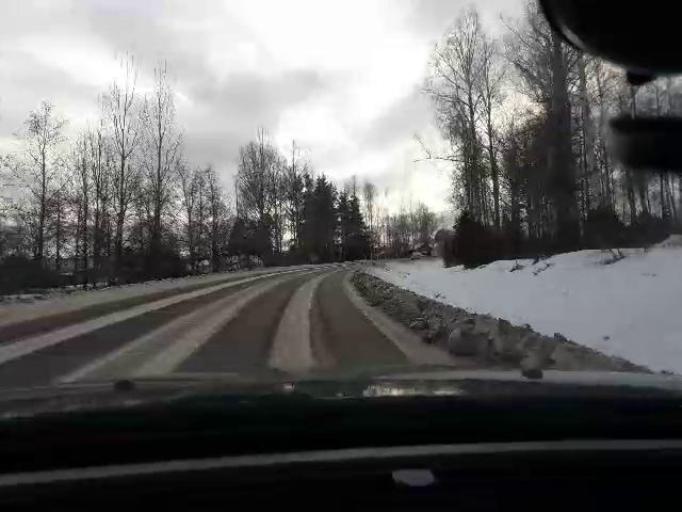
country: SE
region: Gaevleborg
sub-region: Bollnas Kommun
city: Bollnas
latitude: 61.3355
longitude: 16.3928
